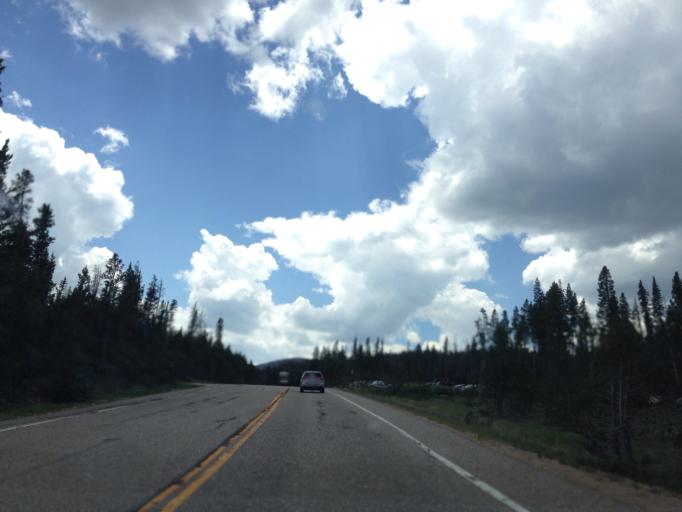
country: US
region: Colorado
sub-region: Larimer County
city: Estes Park
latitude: 40.5803
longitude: -105.8546
